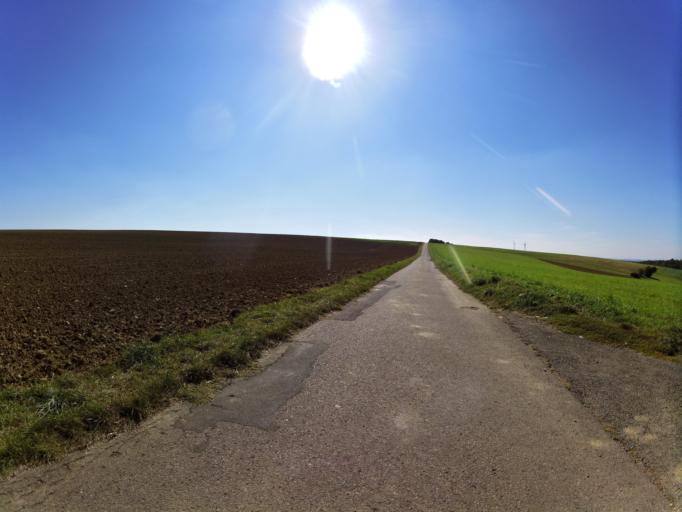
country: DE
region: Bavaria
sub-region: Regierungsbezirk Unterfranken
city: Waldbrunn
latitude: 49.7204
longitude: 9.7940
